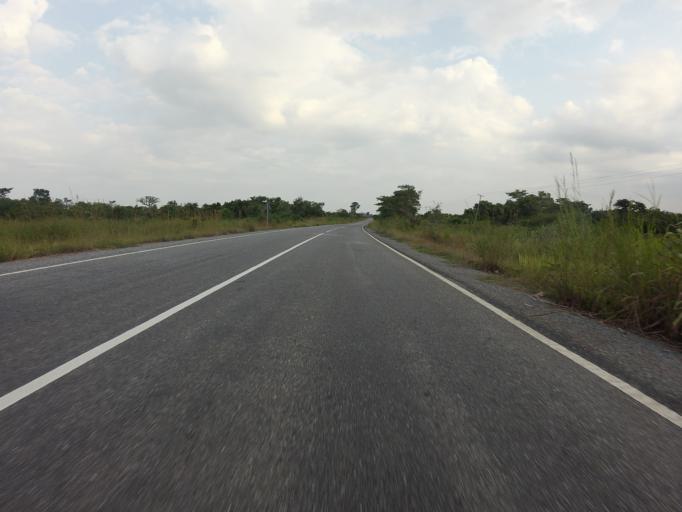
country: GH
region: Volta
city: Ho
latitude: 6.3420
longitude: 0.5394
